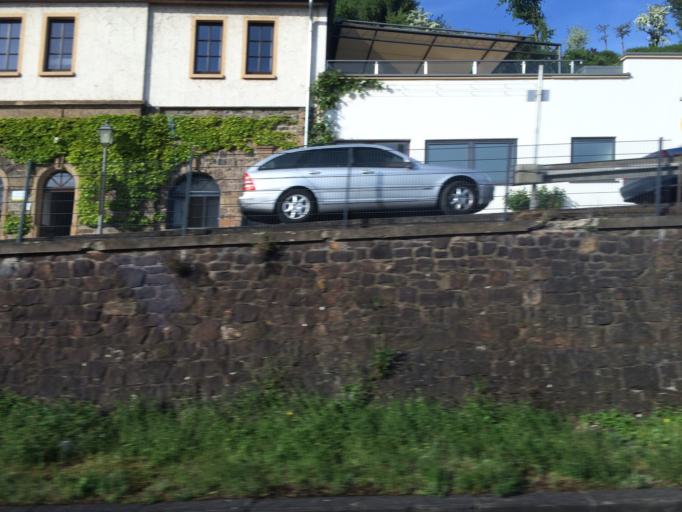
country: DE
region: Rheinland-Pfalz
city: Niederheimbach
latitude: 50.0396
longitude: 7.8144
